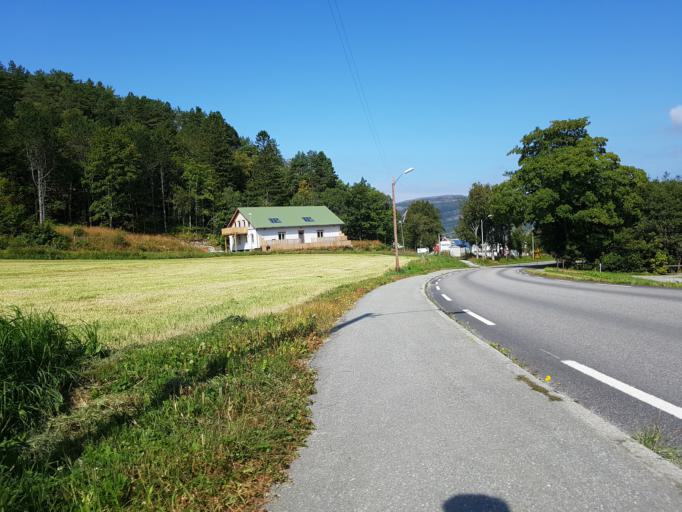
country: NO
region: Sor-Trondelag
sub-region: Agdenes
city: Lensvik
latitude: 63.6297
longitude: 9.8247
